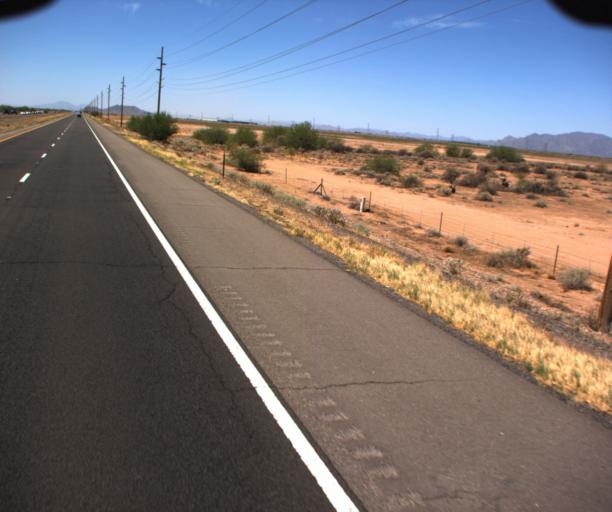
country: US
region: Arizona
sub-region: Maricopa County
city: Sun Lakes
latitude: 33.2383
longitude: -111.9827
